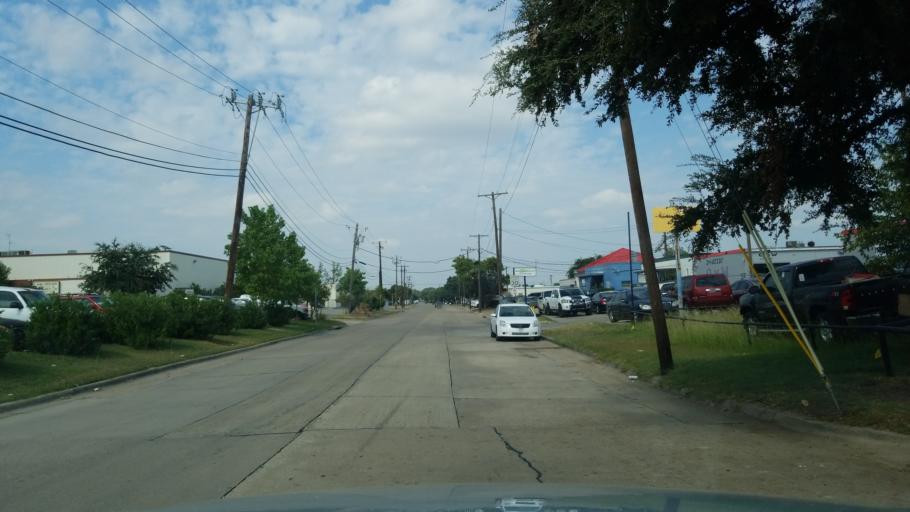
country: US
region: Texas
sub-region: Dallas County
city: Garland
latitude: 32.9095
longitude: -96.6769
